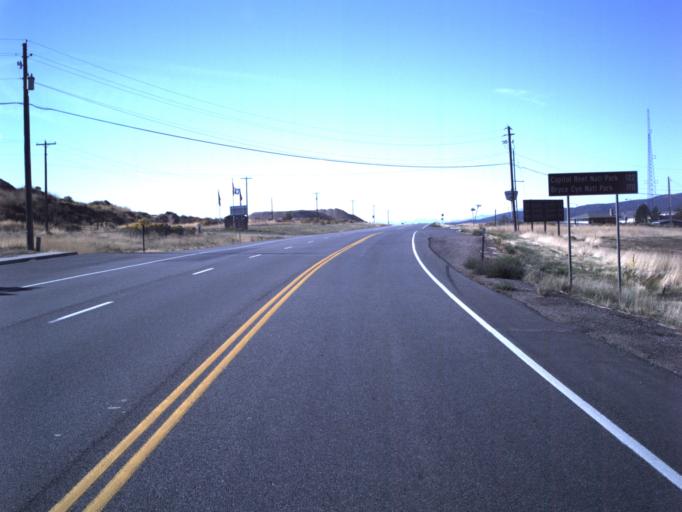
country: US
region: Utah
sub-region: Juab County
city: Nephi
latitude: 39.6761
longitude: -111.8415
